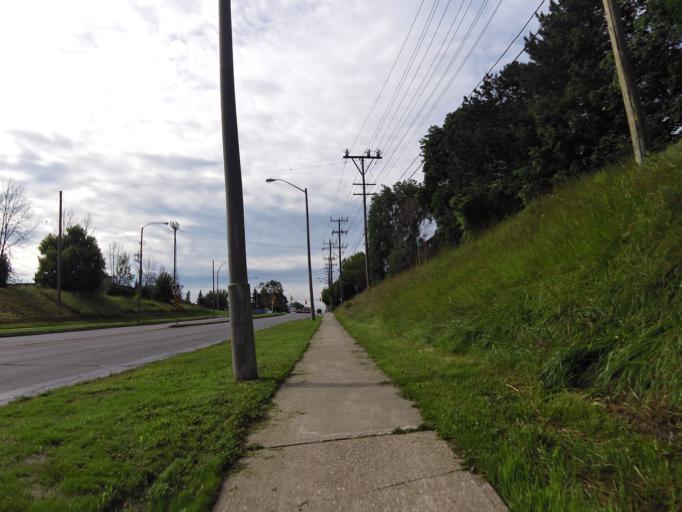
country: CA
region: Ontario
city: Bells Corners
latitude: 45.3333
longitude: -75.7838
